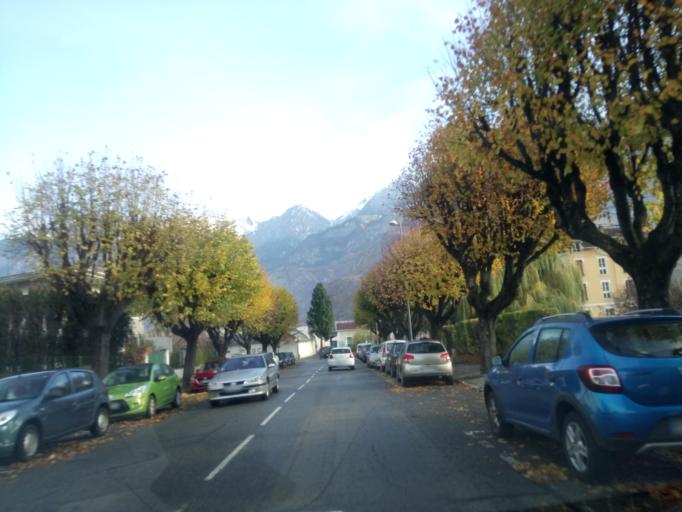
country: FR
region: Rhone-Alpes
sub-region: Departement de la Savoie
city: Saint-Jean-de-Maurienne
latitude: 45.2769
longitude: 6.3534
